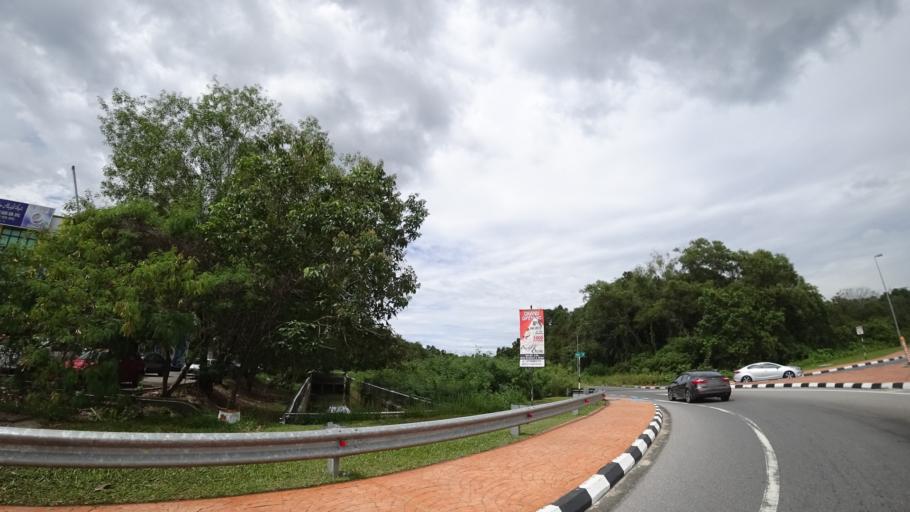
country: BN
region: Brunei and Muara
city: Bandar Seri Begawan
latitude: 4.9011
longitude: 114.9217
